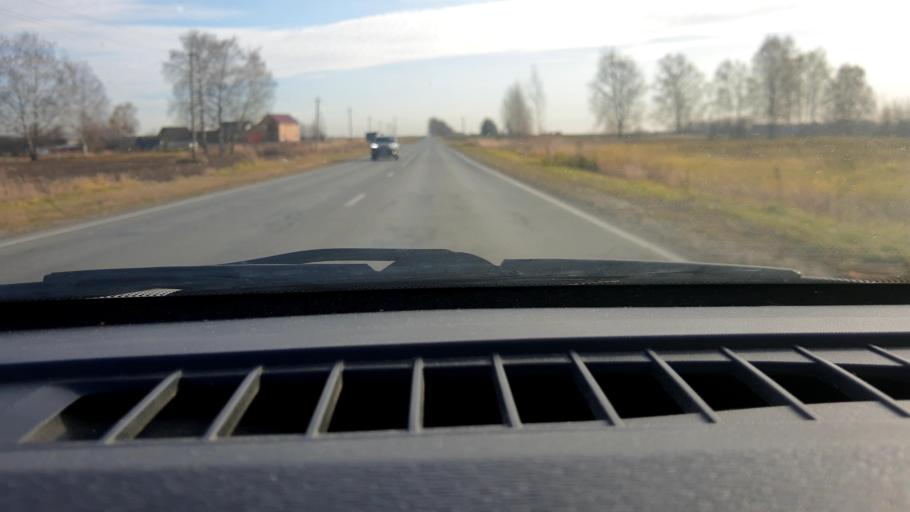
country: RU
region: Nizjnij Novgorod
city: Gorodets
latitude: 56.6312
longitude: 43.5367
